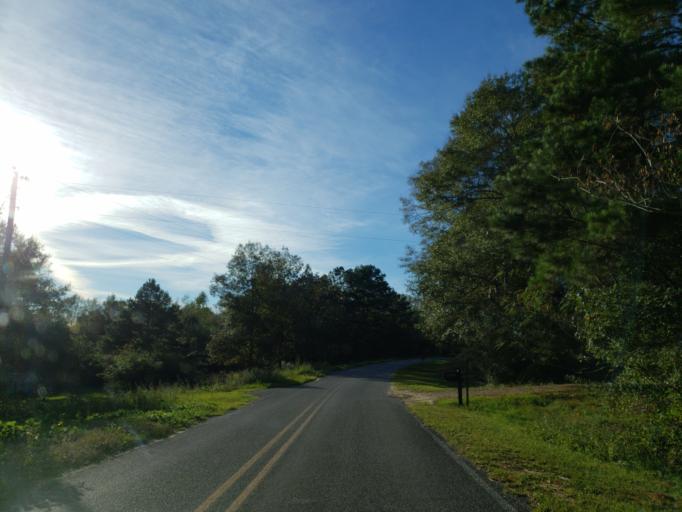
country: US
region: Mississippi
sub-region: Perry County
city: Richton
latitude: 31.3494
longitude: -88.8135
